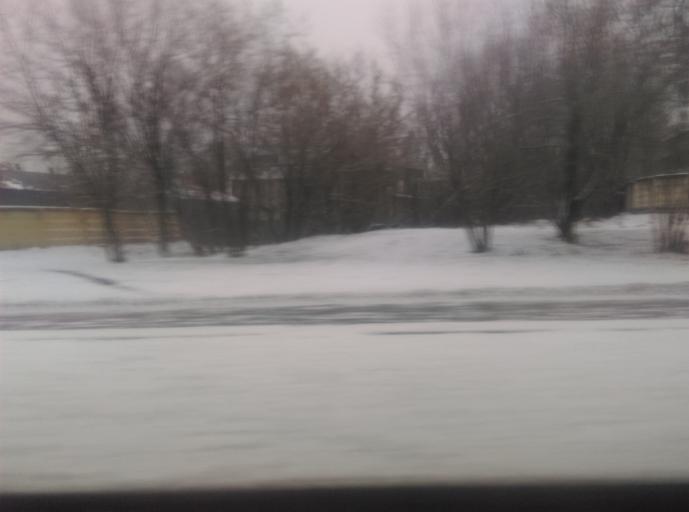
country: RU
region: Moskovskaya
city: Bol'shaya Setun'
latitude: 55.7079
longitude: 37.4217
